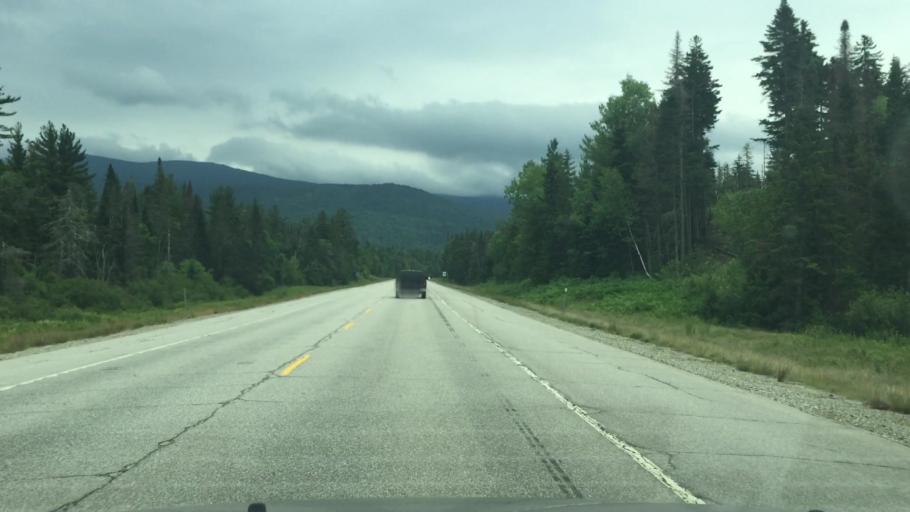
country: US
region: New Hampshire
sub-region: Coos County
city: Jefferson
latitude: 44.2463
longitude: -71.4353
